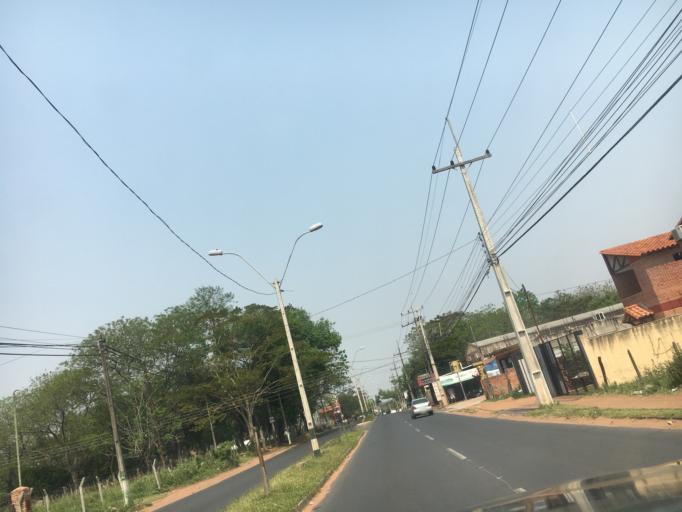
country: PY
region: Central
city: Villa Elisa
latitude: -25.3846
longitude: -57.5841
